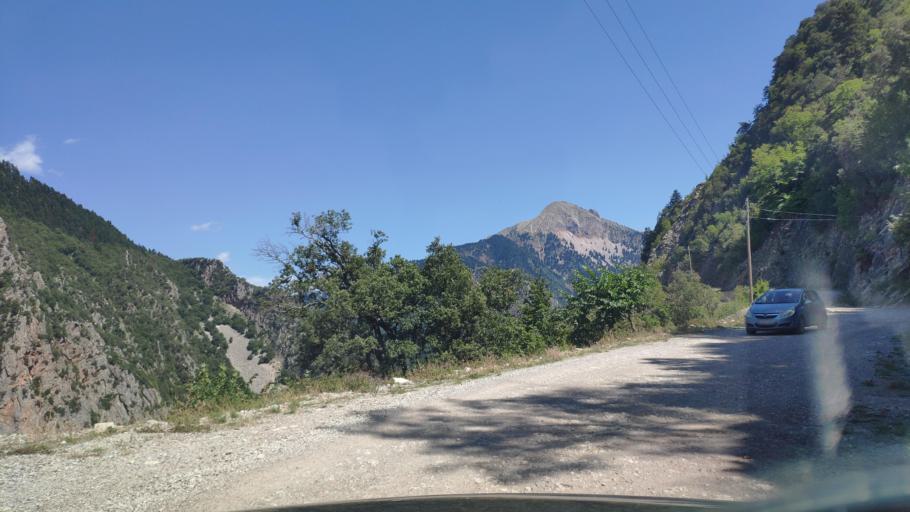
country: GR
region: Central Greece
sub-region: Nomos Evrytanias
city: Kerasochori
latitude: 39.1123
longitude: 21.6159
